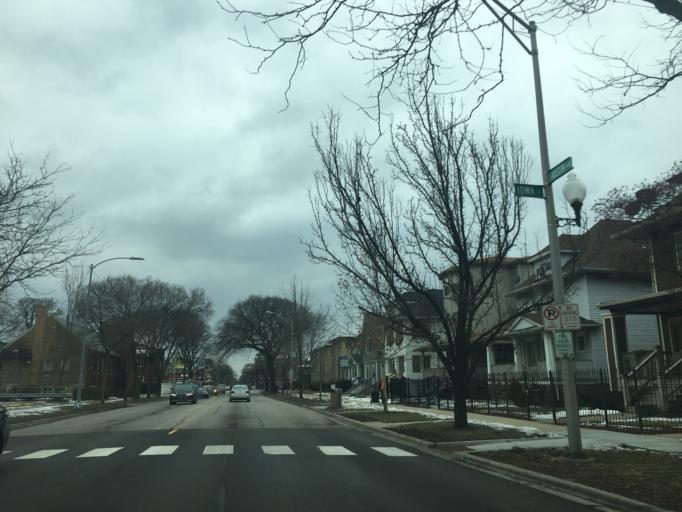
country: US
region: Illinois
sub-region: Cook County
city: Oak Park
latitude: 41.8966
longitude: -87.7752
